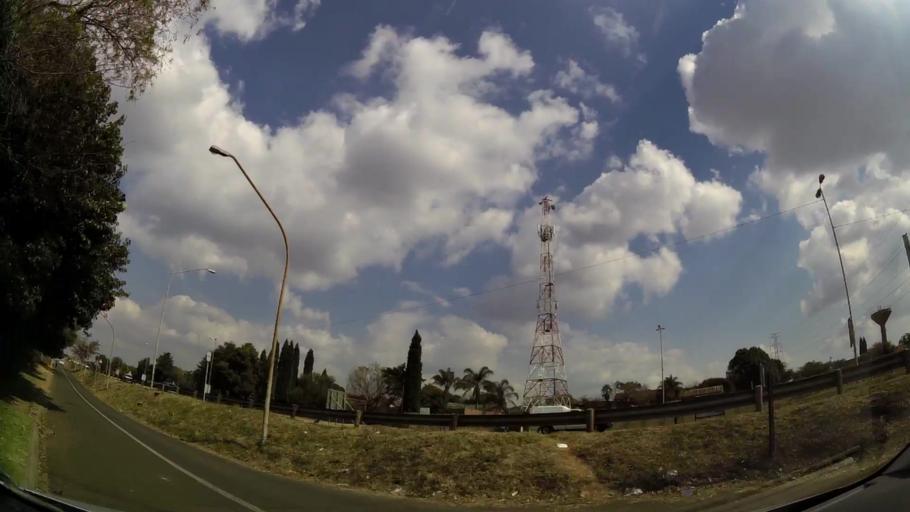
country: ZA
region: Gauteng
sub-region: City of Tshwane Metropolitan Municipality
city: Centurion
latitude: -25.8234
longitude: 28.2557
